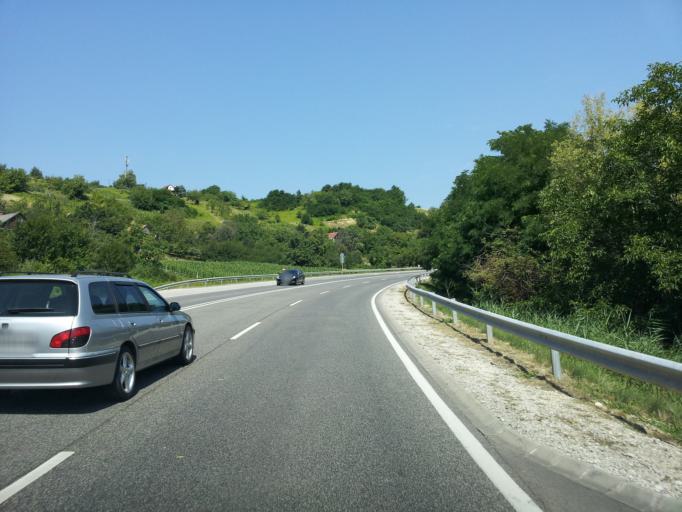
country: HU
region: Zala
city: Pacsa
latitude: 46.8247
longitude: 16.9724
